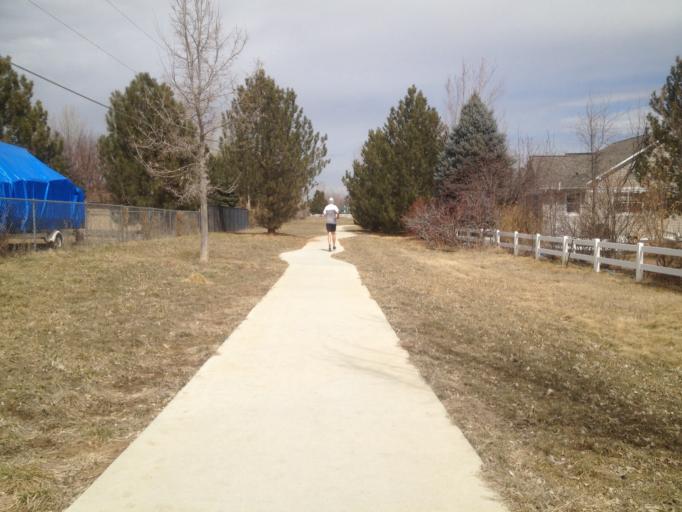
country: US
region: Colorado
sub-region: Boulder County
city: Louisville
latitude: 40.0019
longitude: -105.1404
